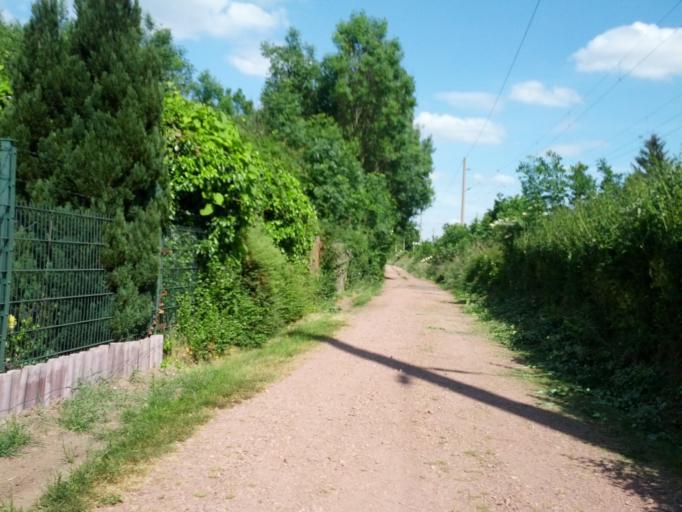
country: DE
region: Thuringia
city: Eisenach
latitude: 50.9784
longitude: 10.2892
